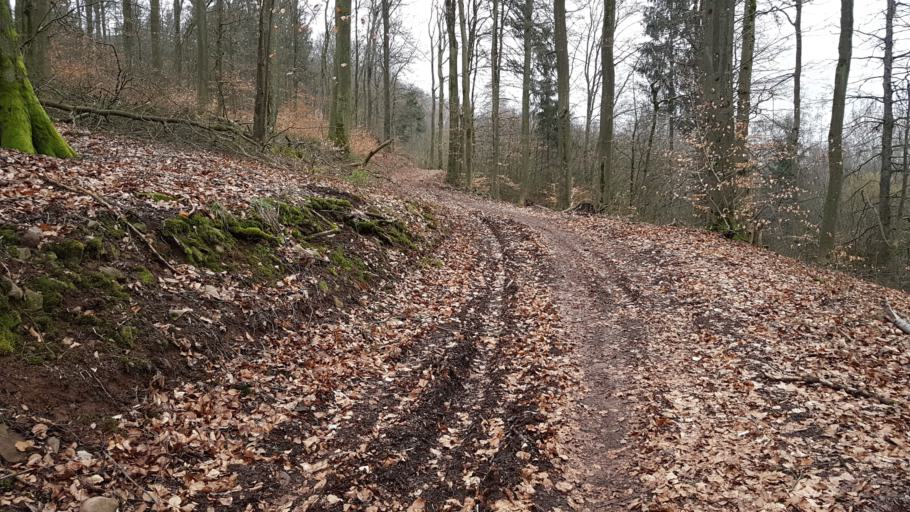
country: DE
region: Saarland
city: Sankt Wendel
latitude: 49.4410
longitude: 7.1711
